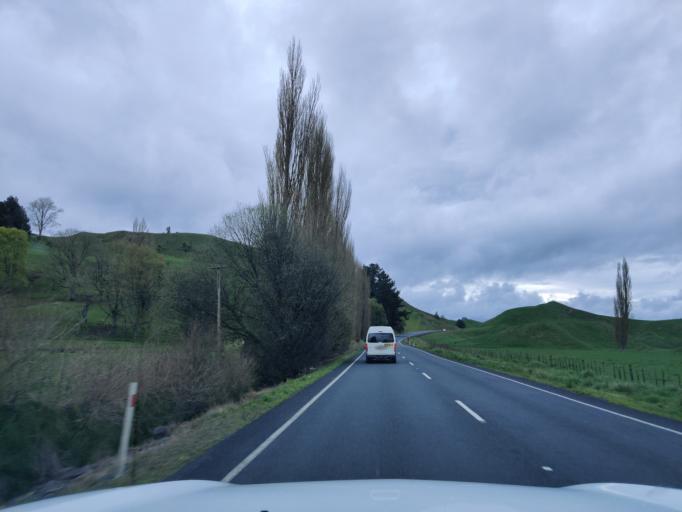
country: NZ
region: Waikato
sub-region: Otorohanga District
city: Otorohanga
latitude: -38.4714
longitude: 175.1722
